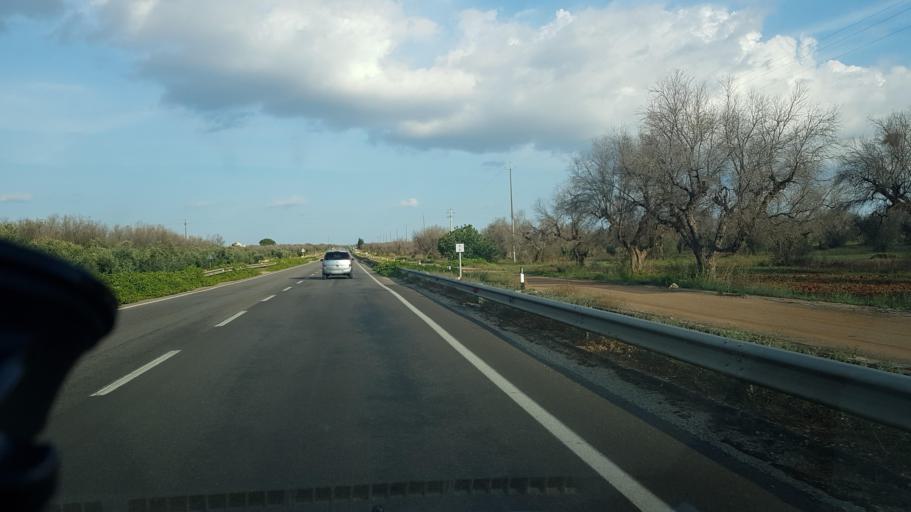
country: IT
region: Apulia
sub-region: Provincia di Lecce
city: Gemini
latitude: 39.9209
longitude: 18.1956
